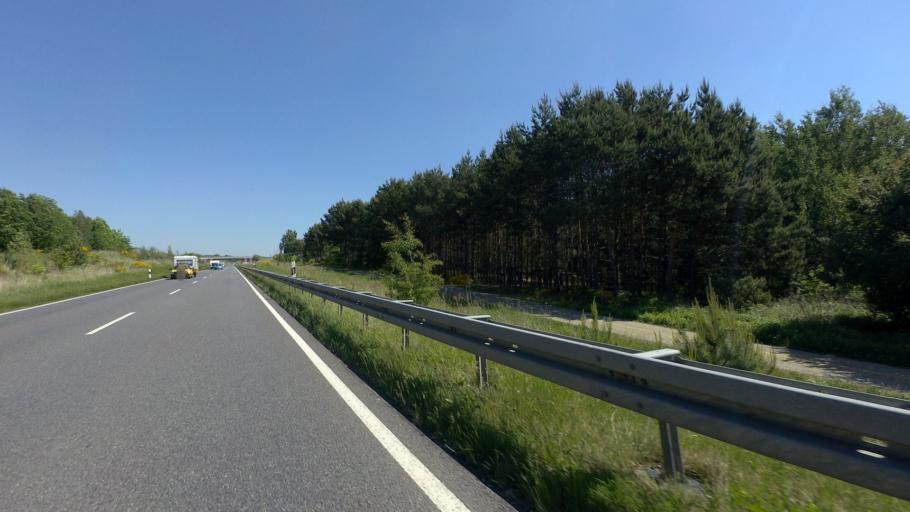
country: DE
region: Brandenburg
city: Spremberg
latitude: 51.5667
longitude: 14.3311
